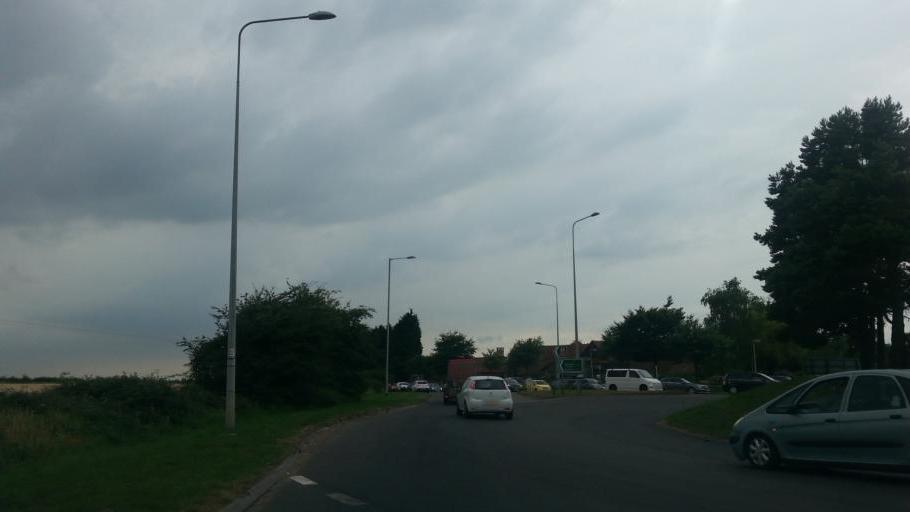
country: GB
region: England
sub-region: Norfolk
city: Dersingham
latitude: 52.7786
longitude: 0.4718
